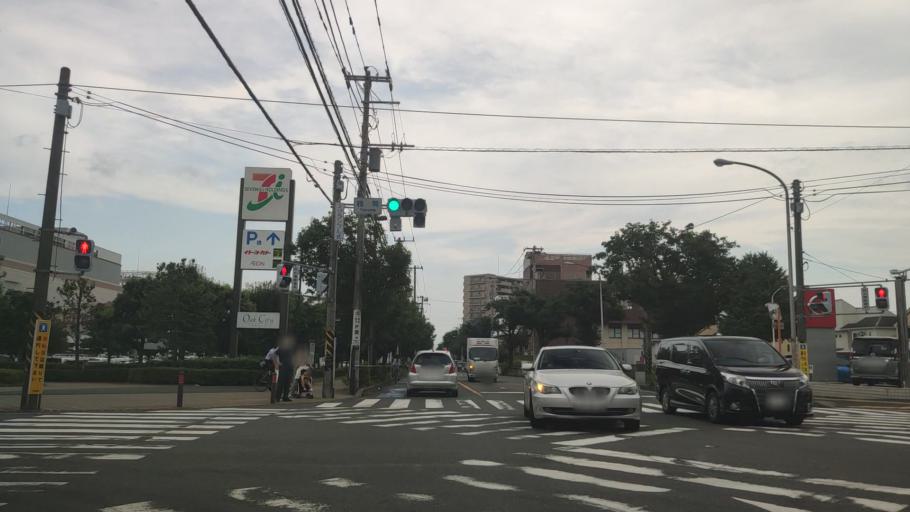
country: JP
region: Kanagawa
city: Minami-rinkan
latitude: 35.4912
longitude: 139.4554
